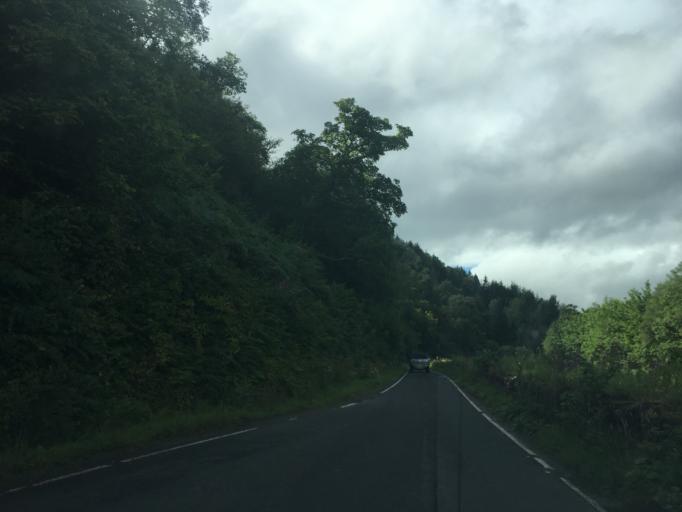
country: GB
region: Scotland
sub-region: Argyll and Bute
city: Ardrishaig
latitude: 56.0795
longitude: -5.5483
